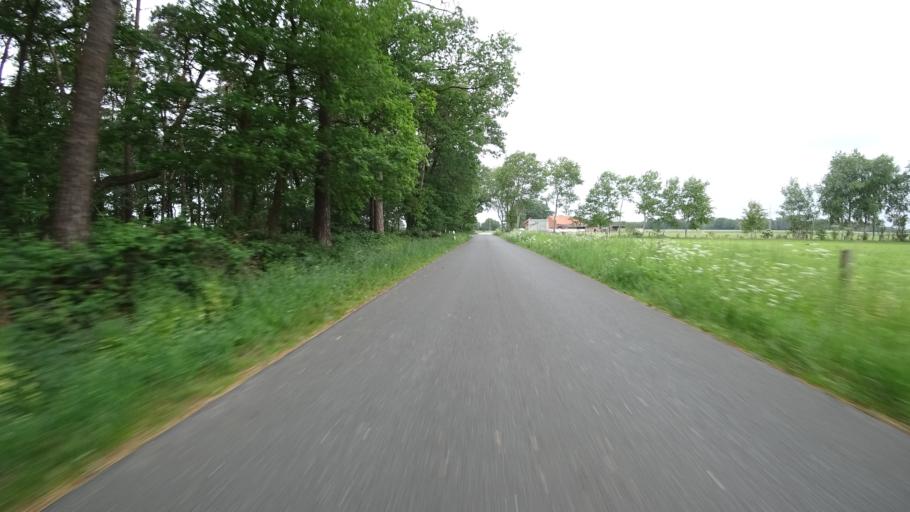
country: DE
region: North Rhine-Westphalia
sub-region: Regierungsbezirk Detmold
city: Rheda-Wiedenbruck
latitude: 51.8443
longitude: 8.3405
